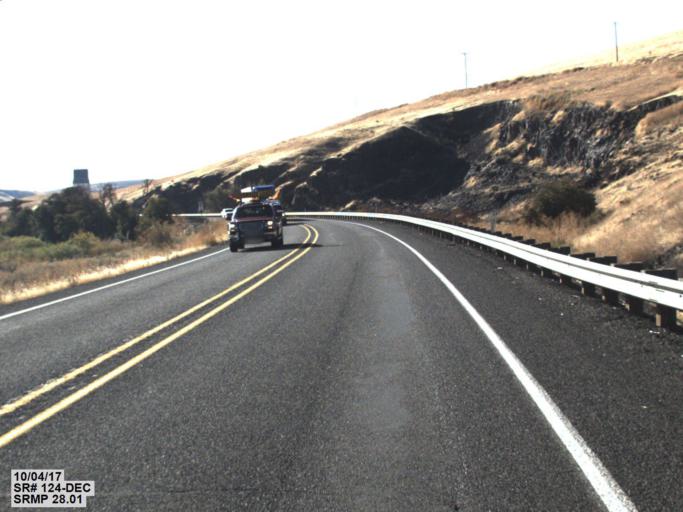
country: US
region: Washington
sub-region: Walla Walla County
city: Garrett
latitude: 46.2906
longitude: -118.4769
